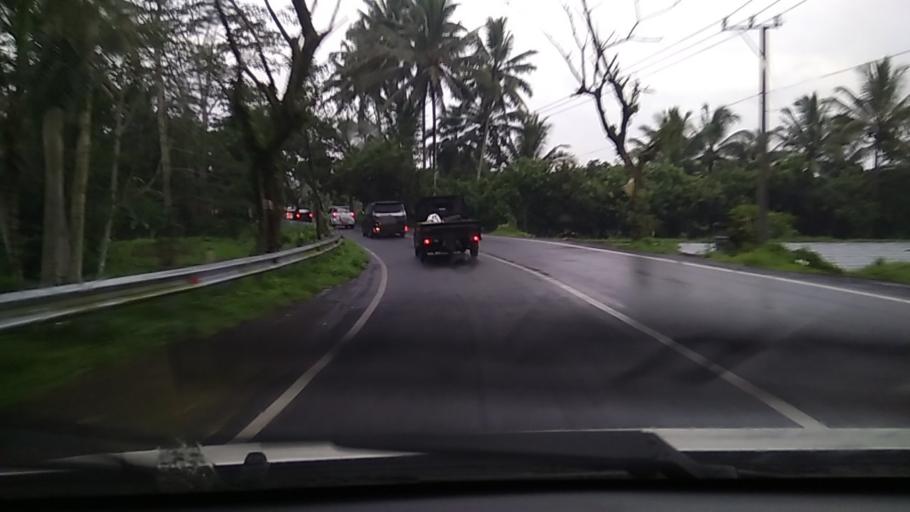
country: ID
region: Bali
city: Pergan
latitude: -8.4159
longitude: 115.1982
